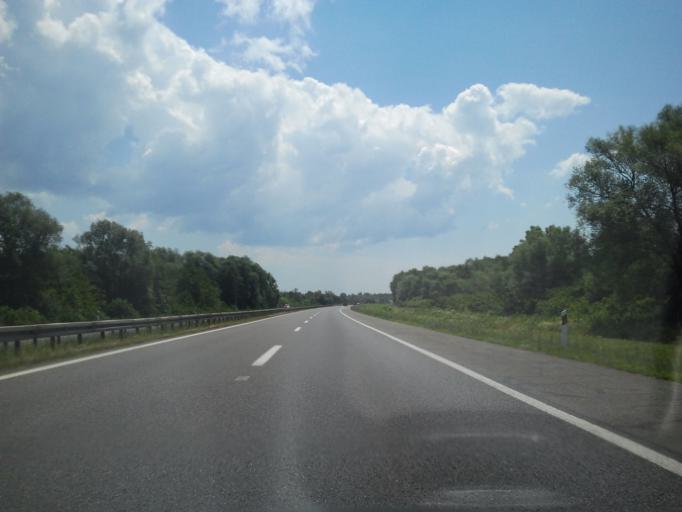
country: HR
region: Zagrebacka
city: Novoselec
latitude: 45.6144
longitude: 16.5414
